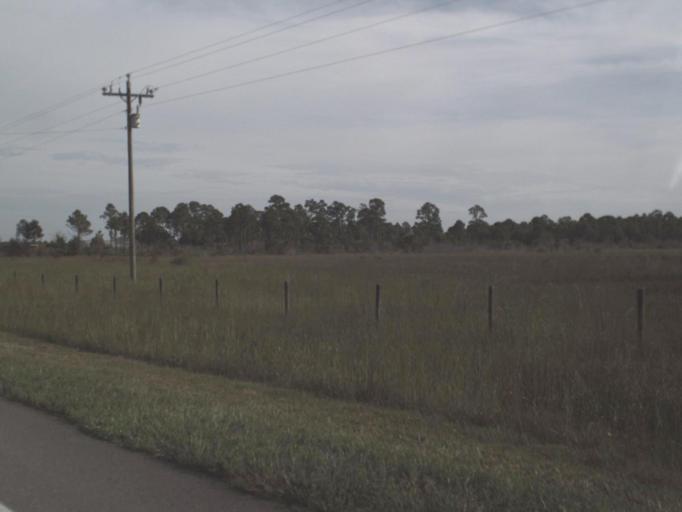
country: US
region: Florida
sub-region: Lee County
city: Fort Myers Shores
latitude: 26.8059
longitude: -81.7603
